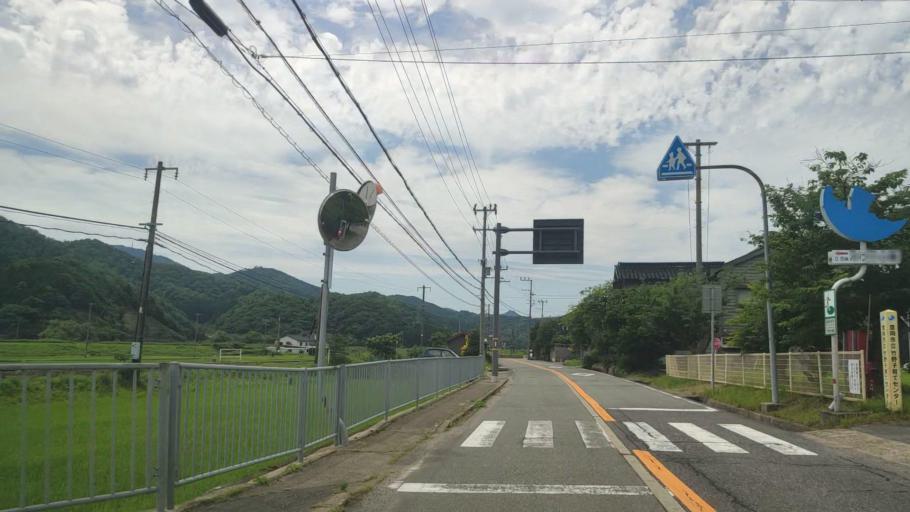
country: JP
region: Hyogo
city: Toyooka
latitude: 35.6432
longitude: 134.7581
